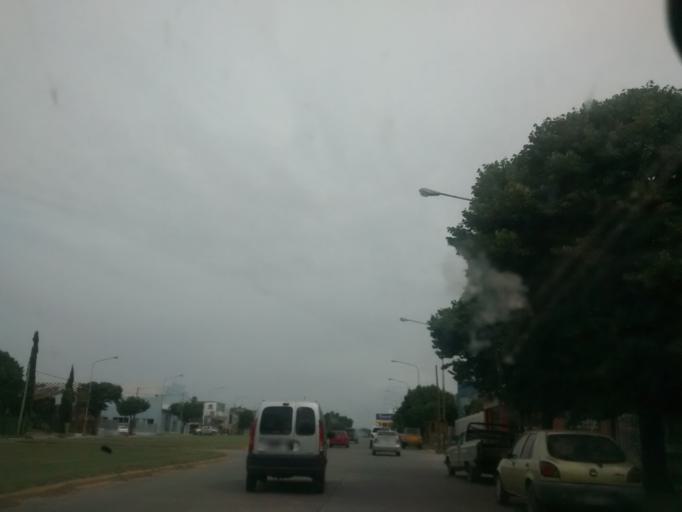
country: AR
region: Buenos Aires
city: Necochea
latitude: -38.5688
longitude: -58.7204
